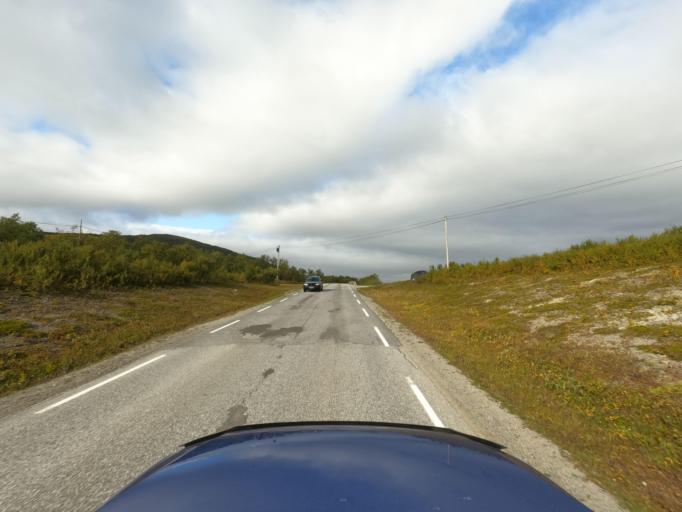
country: NO
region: Finnmark Fylke
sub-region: Porsanger
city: Lakselv
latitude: 70.2908
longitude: 25.0713
